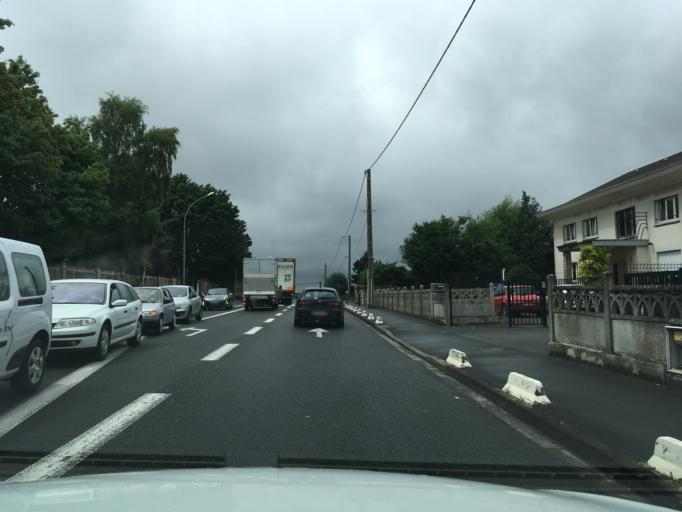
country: FR
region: Picardie
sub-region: Departement de l'Aisne
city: Harly
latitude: 49.8410
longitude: 3.3225
